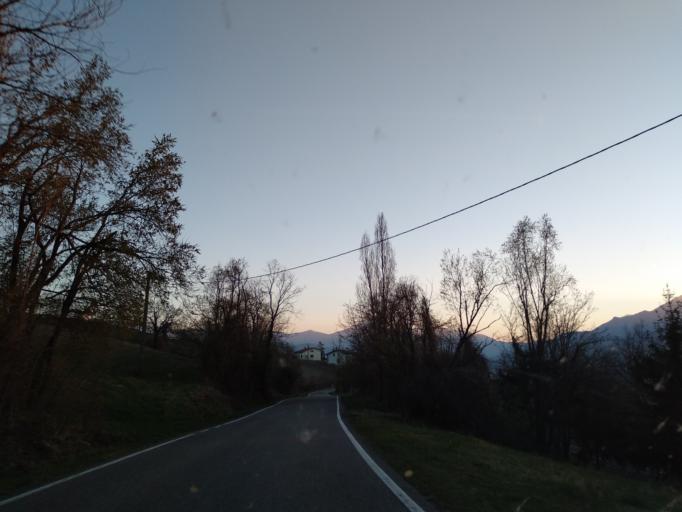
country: IT
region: Emilia-Romagna
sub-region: Provincia di Reggio Emilia
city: Castelnovo ne'Monti
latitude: 44.4180
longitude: 10.4036
